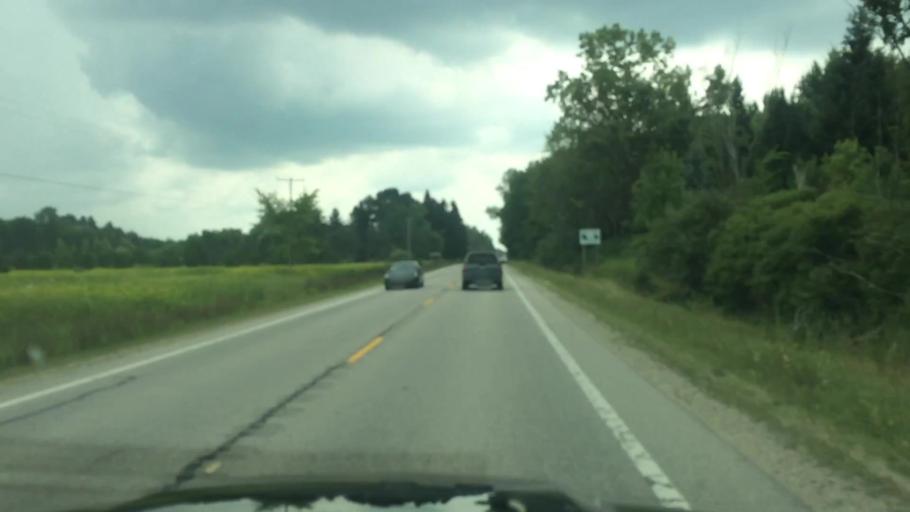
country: US
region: Michigan
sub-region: Tuscola County
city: Cass City
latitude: 43.5014
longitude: -83.0919
